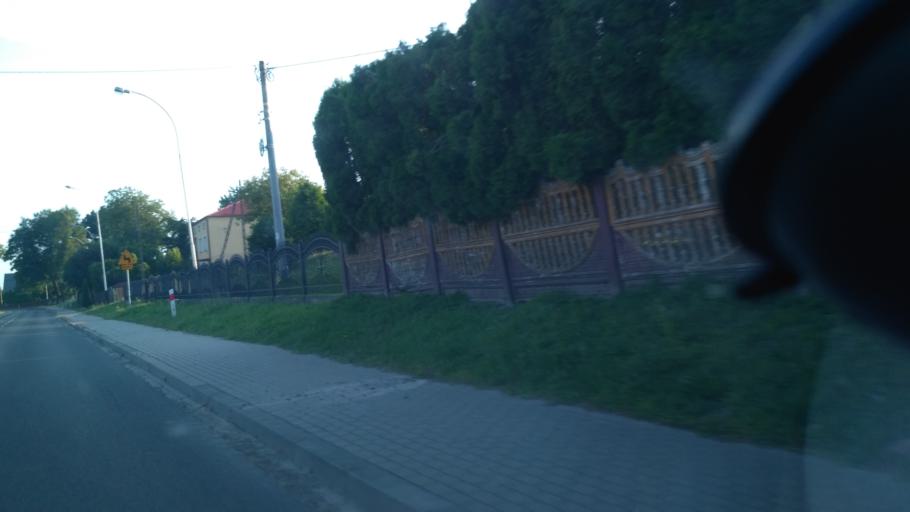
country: PL
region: Subcarpathian Voivodeship
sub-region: Powiat lezajski
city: Stare Miasto
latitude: 50.2795
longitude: 22.4287
